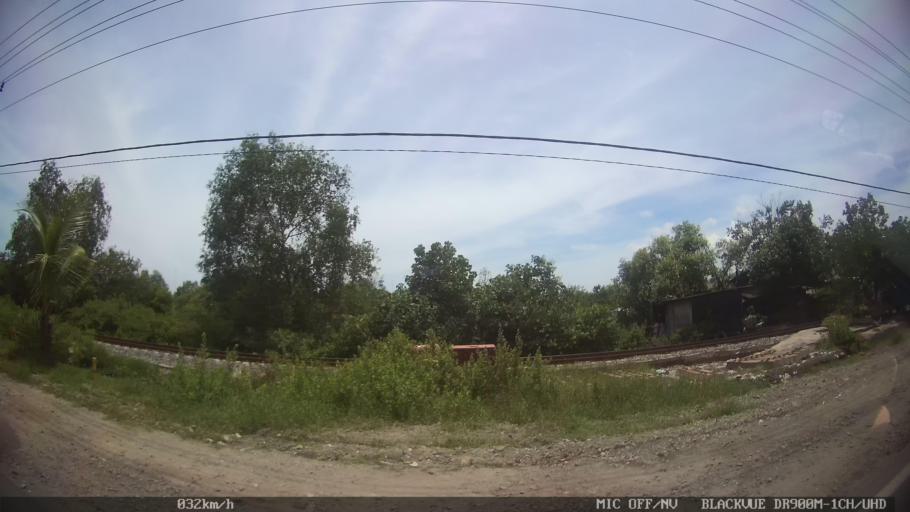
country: ID
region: North Sumatra
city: Belawan
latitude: 3.7667
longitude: 98.6828
